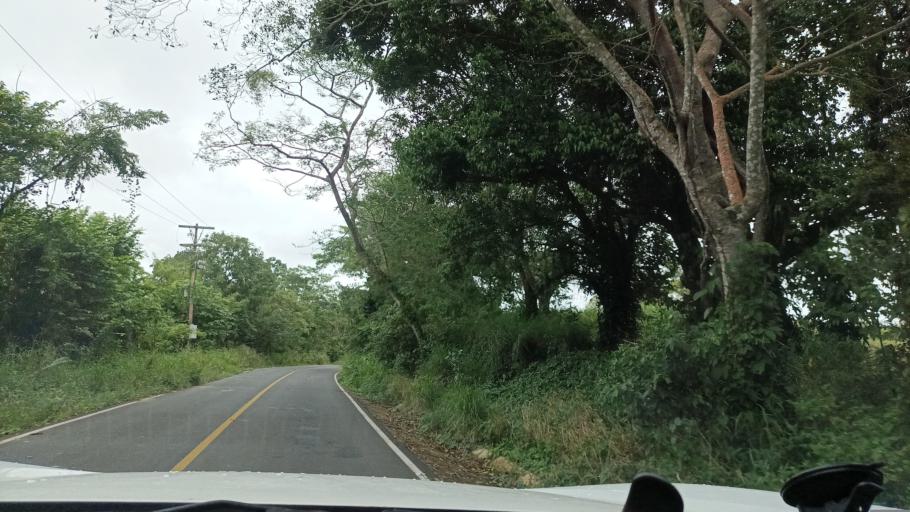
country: MX
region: Veracruz
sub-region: Moloacan
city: Cuichapa
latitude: 17.7990
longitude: -94.3582
